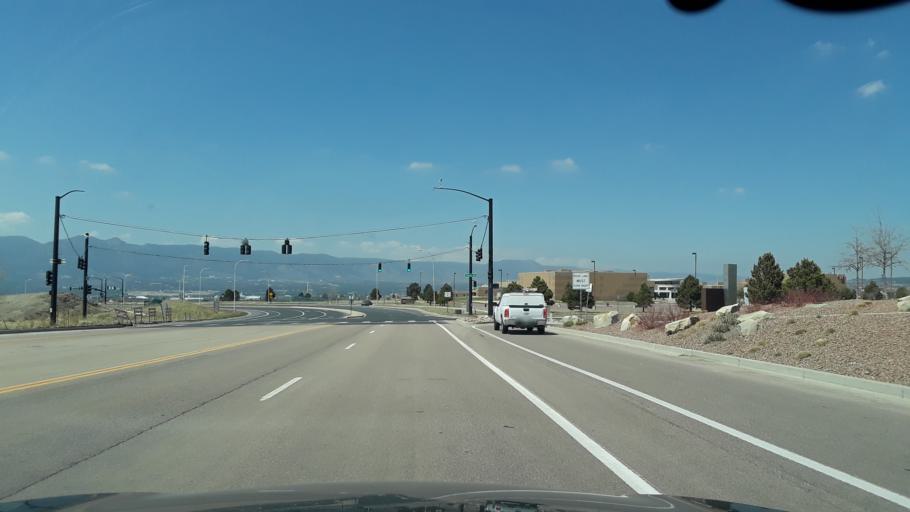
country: US
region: Colorado
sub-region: El Paso County
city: Black Forest
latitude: 38.9847
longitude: -104.7600
